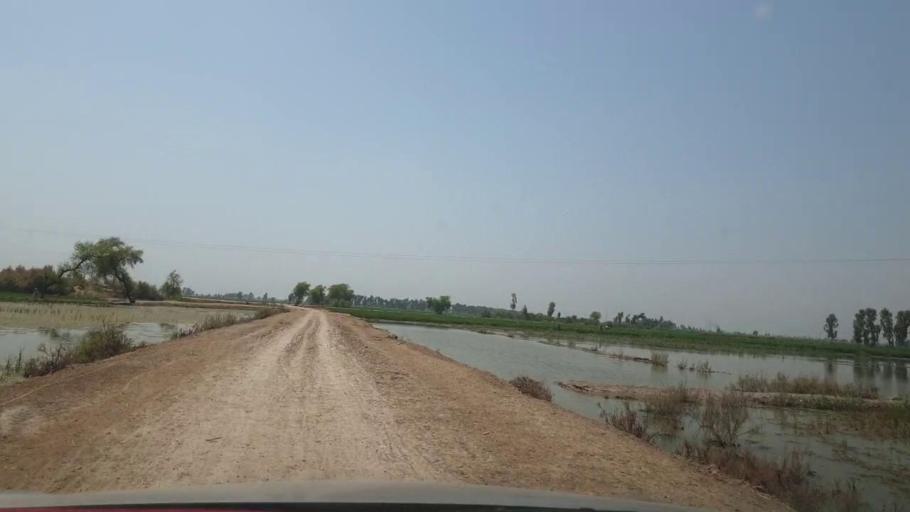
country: PK
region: Sindh
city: Warah
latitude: 27.5156
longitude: 67.7772
